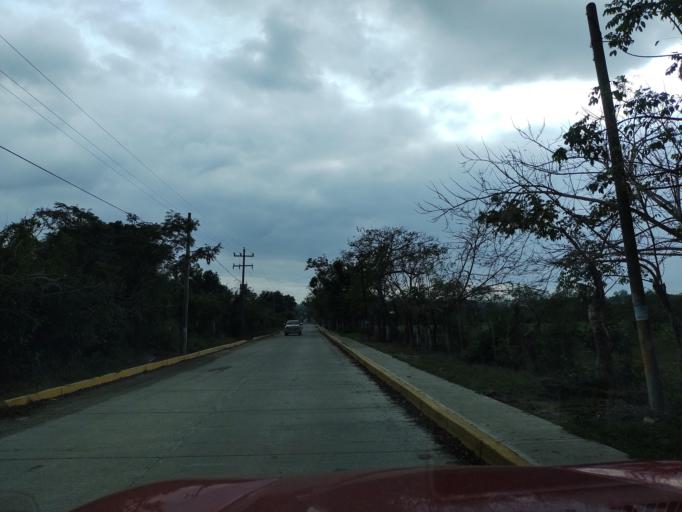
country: MX
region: Veracruz
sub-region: Papantla
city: El Chote
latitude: 20.4340
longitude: -97.3801
